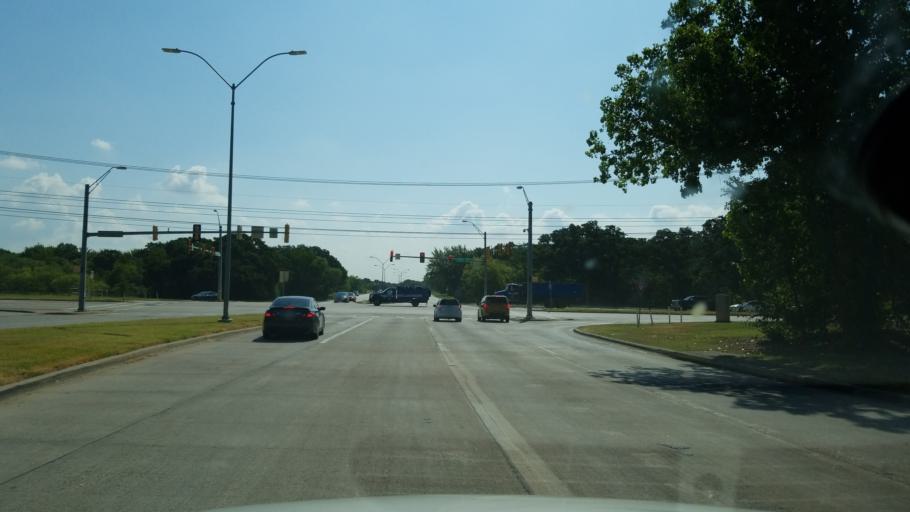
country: US
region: Texas
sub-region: Tarrant County
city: Euless
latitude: 32.8166
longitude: -97.1005
